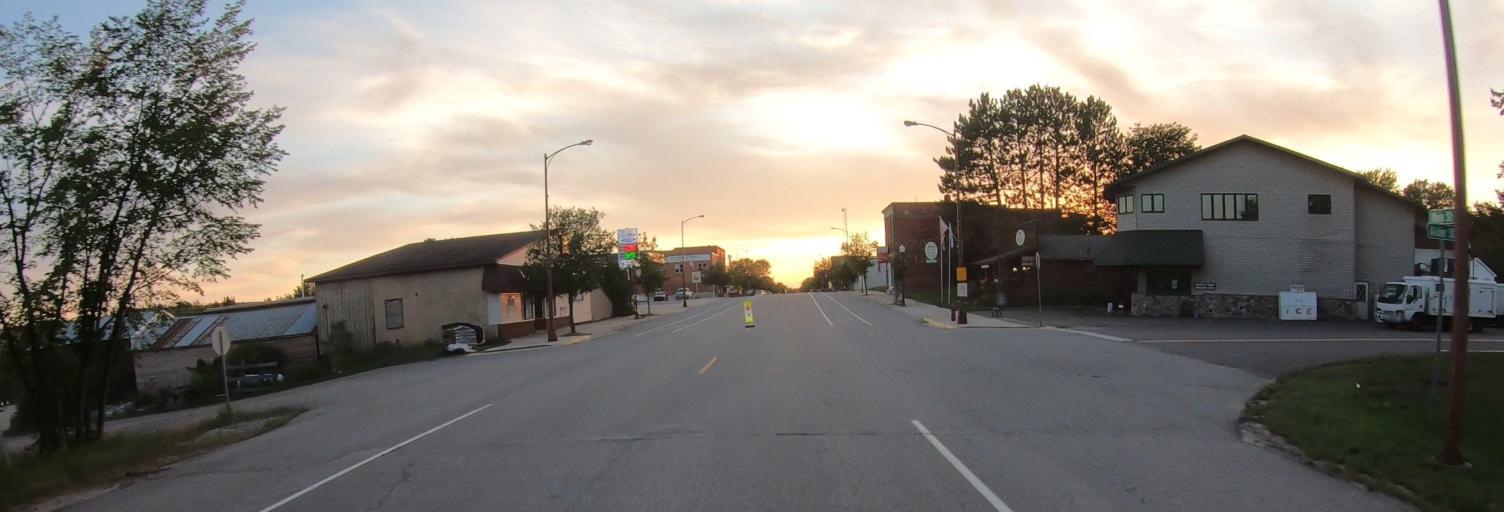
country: US
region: Minnesota
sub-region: Saint Louis County
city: Aurora
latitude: 47.8052
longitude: -92.2702
